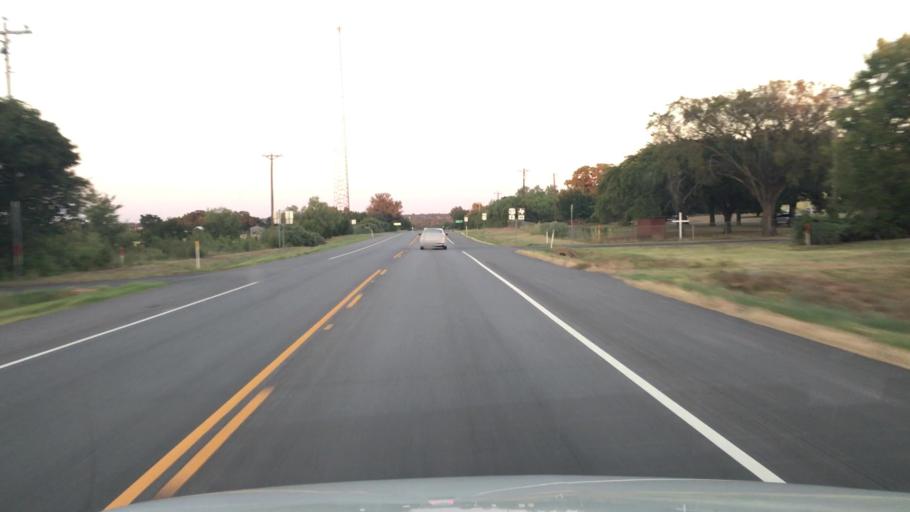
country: US
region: Texas
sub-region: Somervell County
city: Glen Rose
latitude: 32.1918
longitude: -97.8375
